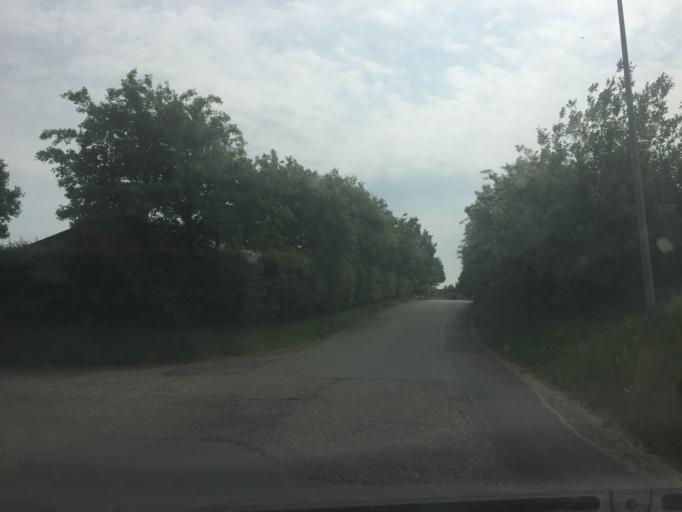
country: DK
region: South Denmark
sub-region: Kolding Kommune
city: Sonder Bjert
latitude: 55.4631
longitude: 9.5519
